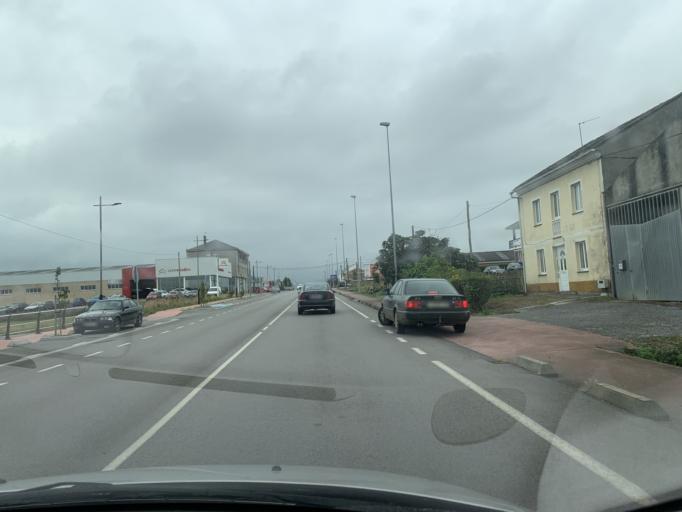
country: ES
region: Galicia
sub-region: Provincia de Lugo
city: Ribadeo
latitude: 43.5406
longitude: -7.0659
